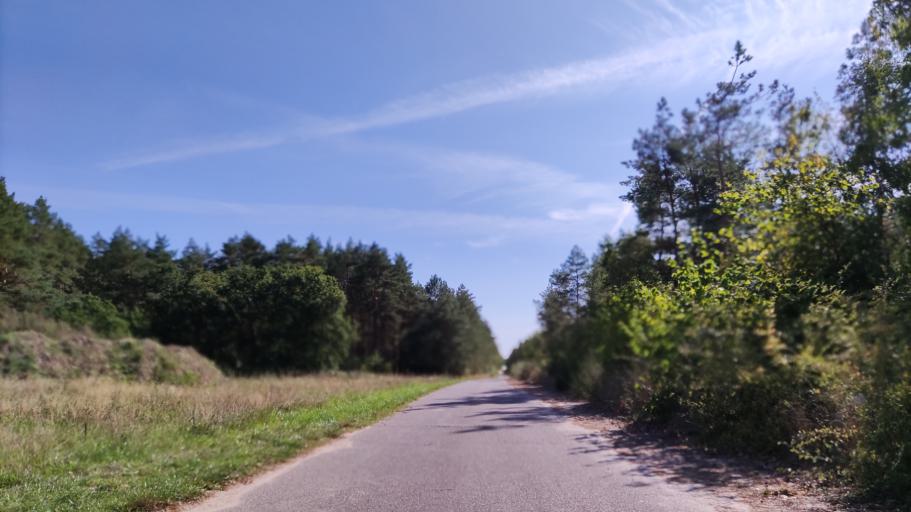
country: DE
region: Lower Saxony
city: Wendisch Evern
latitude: 53.2146
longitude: 10.4952
